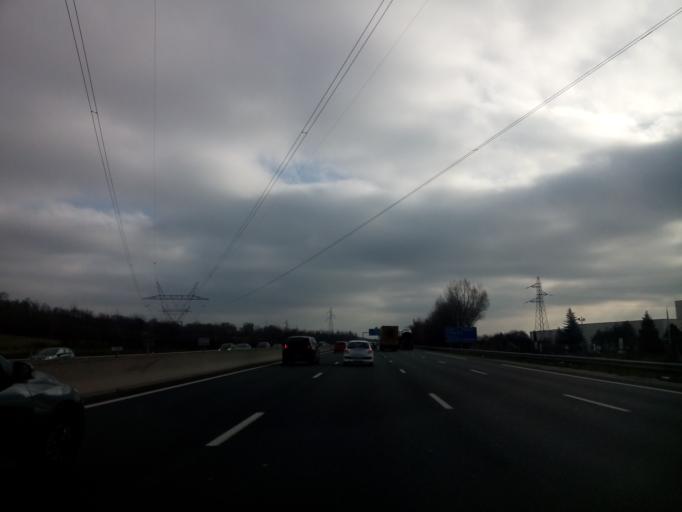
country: FR
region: Rhone-Alpes
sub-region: Departement du Rhone
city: Saint-Laurent-de-Mure
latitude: 45.6778
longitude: 5.0283
